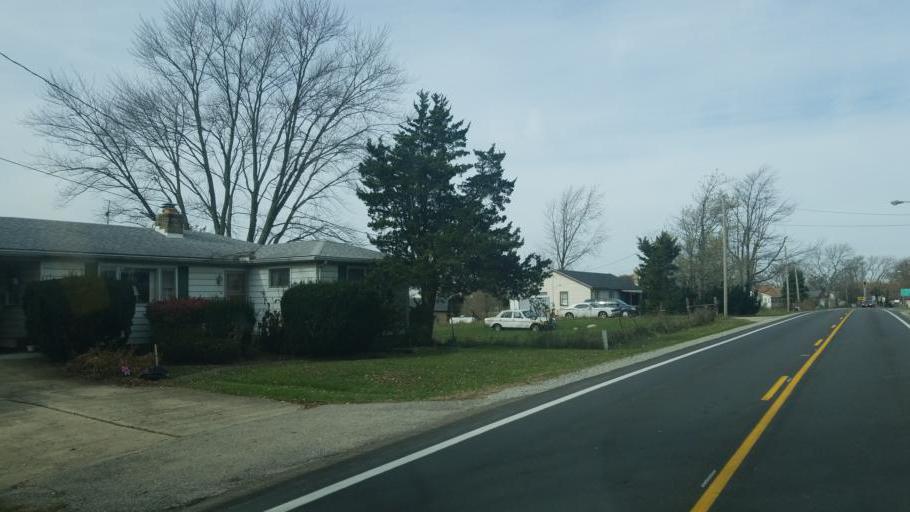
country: US
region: Ohio
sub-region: Madison County
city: Choctaw Lake
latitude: 39.9311
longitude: -83.4909
